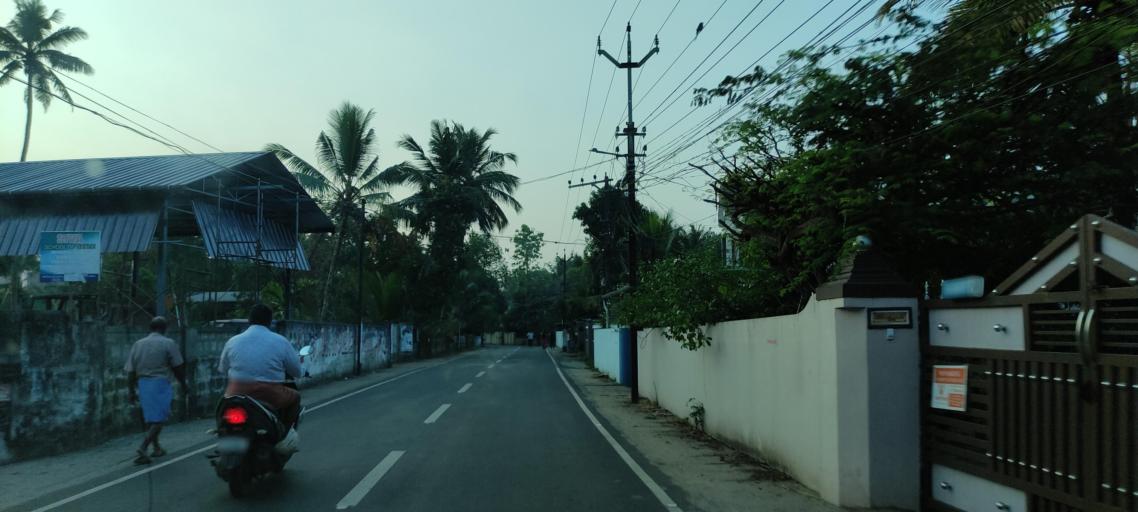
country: IN
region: Kerala
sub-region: Alappuzha
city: Alleppey
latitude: 9.4652
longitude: 76.3429
